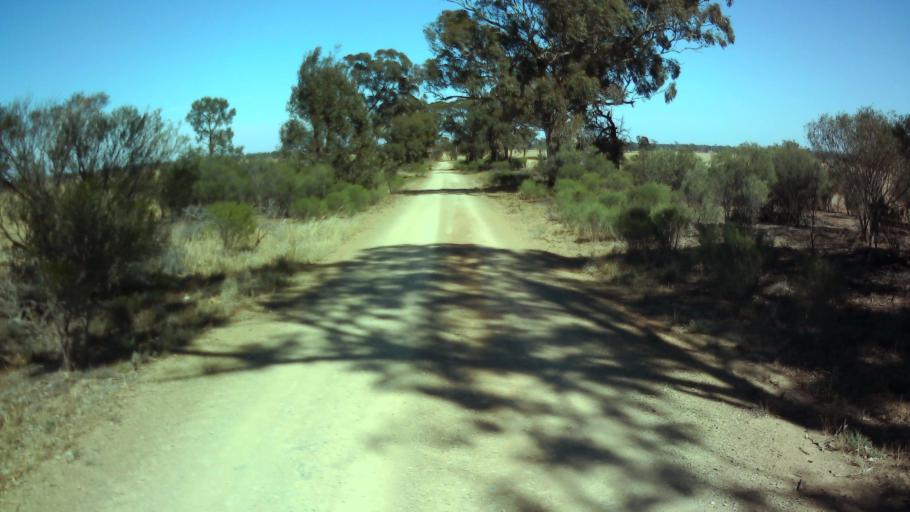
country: AU
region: New South Wales
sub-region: Weddin
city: Grenfell
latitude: -33.8796
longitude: 147.8788
